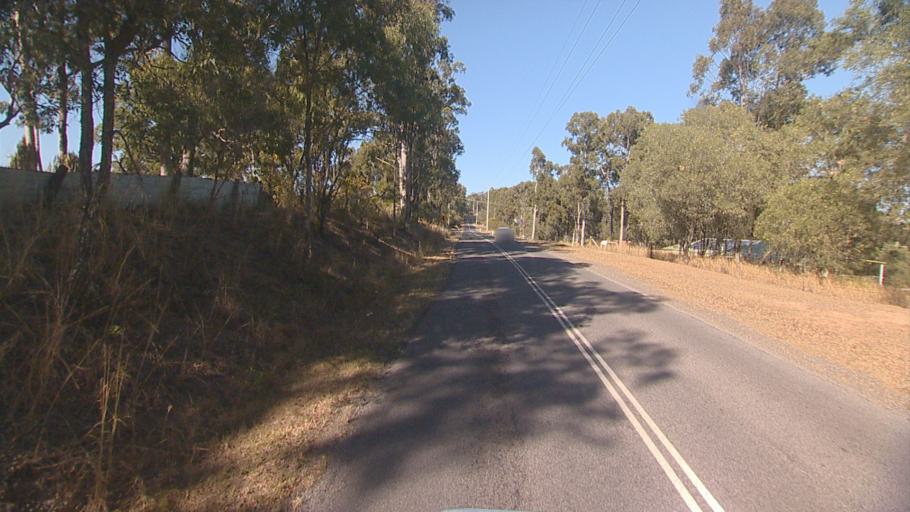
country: AU
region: Queensland
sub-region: Logan
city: Cedar Vale
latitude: -27.8813
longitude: 153.0156
